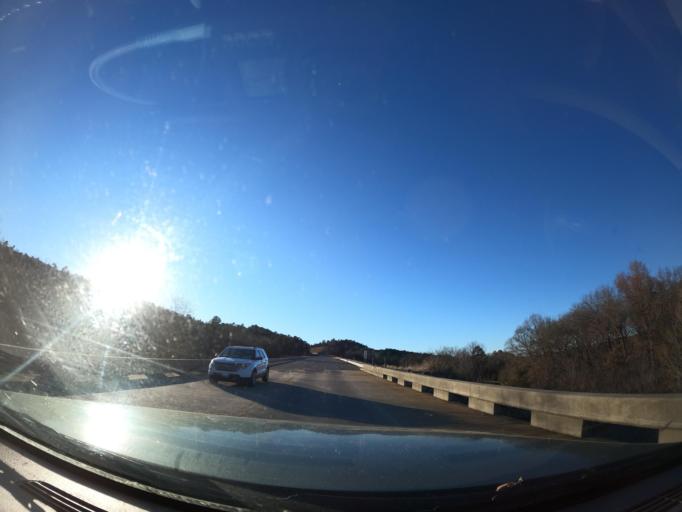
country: US
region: Oklahoma
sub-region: Pittsburg County
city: Hartshorne
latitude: 34.8914
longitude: -95.4487
